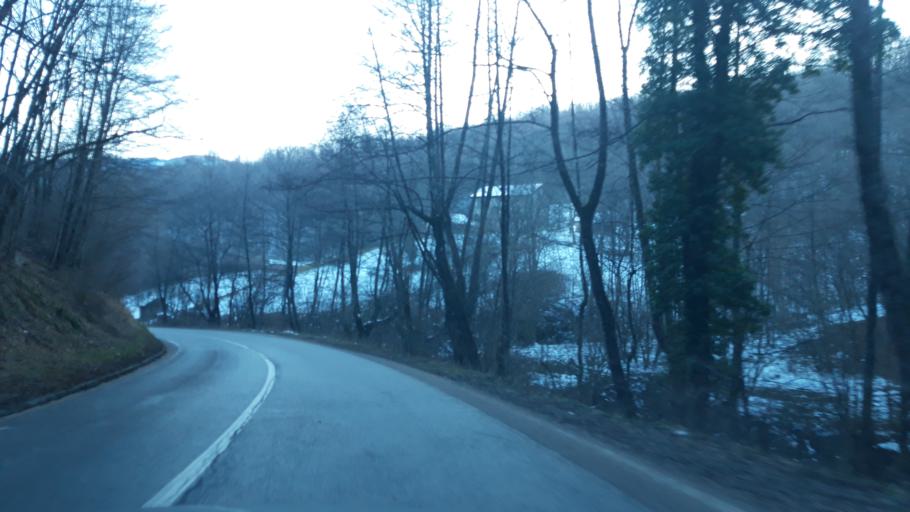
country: BA
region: Republika Srpska
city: Vlasenica
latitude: 44.1796
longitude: 19.0090
